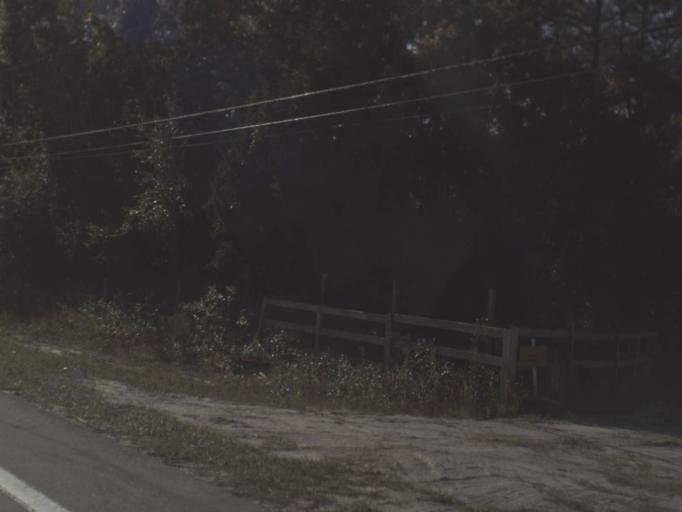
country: US
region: Florida
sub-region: Volusia County
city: Samsula-Spruce Creek
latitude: 29.0940
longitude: -81.0480
